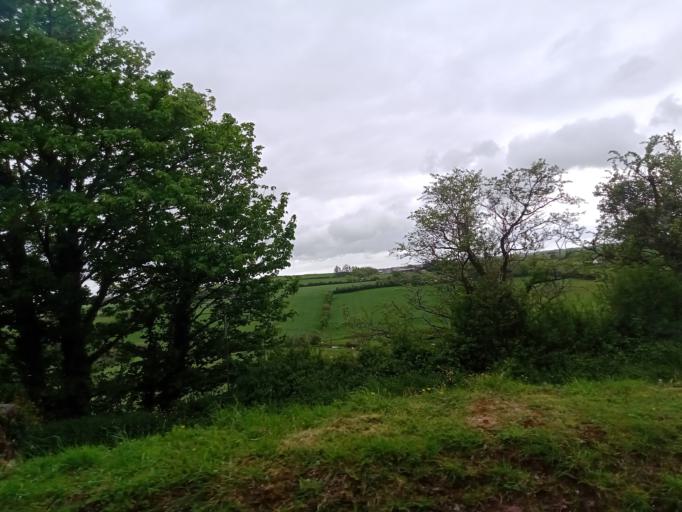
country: IE
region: Munster
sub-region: County Cork
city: Kinsale
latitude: 51.8109
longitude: -8.5461
